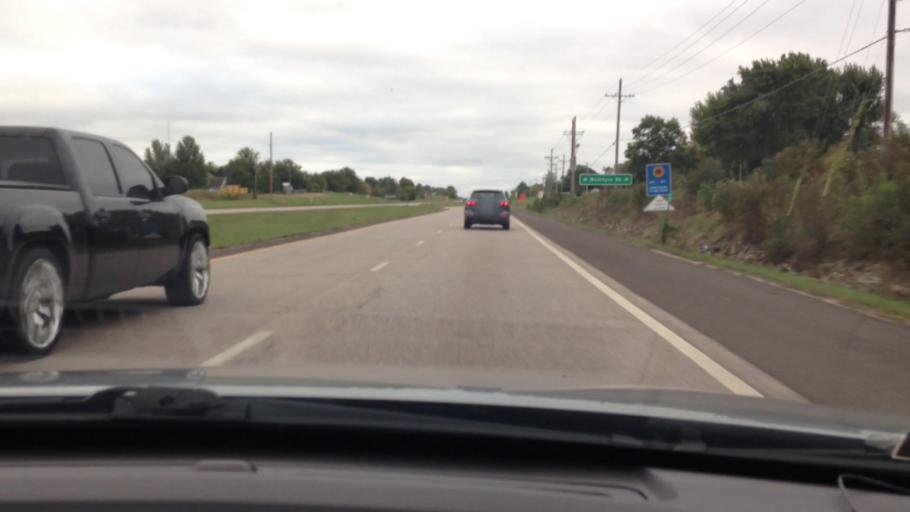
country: US
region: Kansas
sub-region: Leavenworth County
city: Lansing
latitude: 39.2182
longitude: -94.9004
